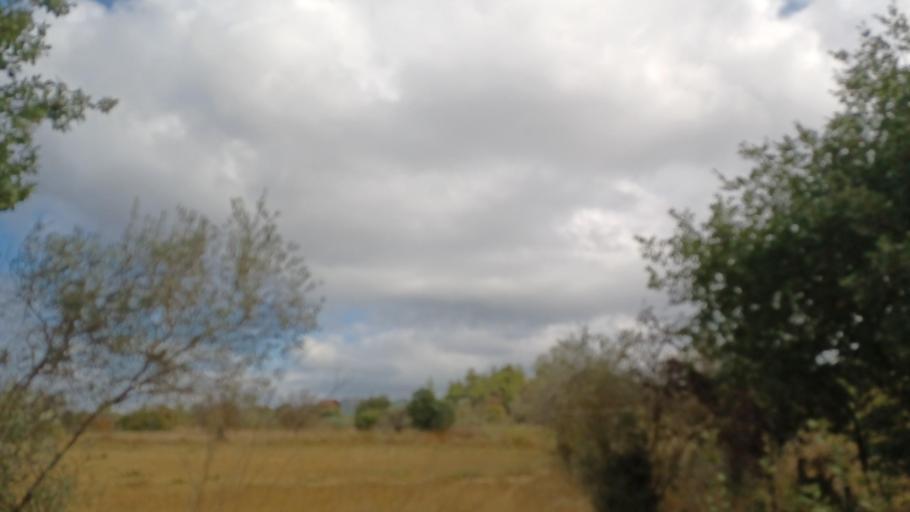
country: CY
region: Pafos
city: Polis
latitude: 35.0058
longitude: 32.4968
